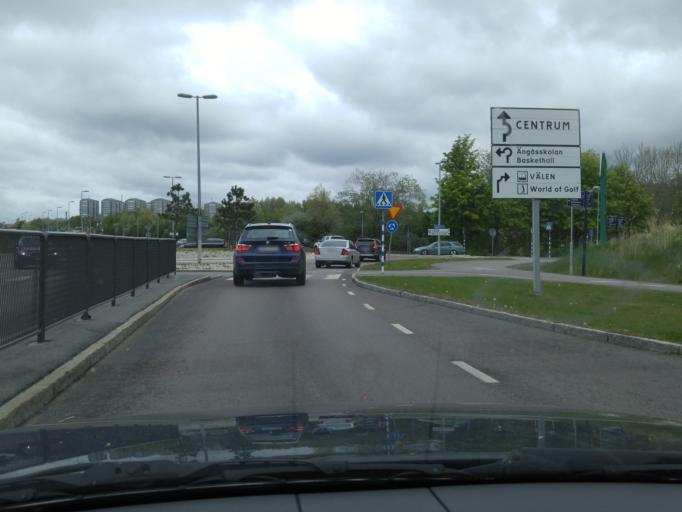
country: SE
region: Vaestra Goetaland
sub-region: Goteborg
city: Majorna
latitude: 57.6434
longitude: 11.9170
